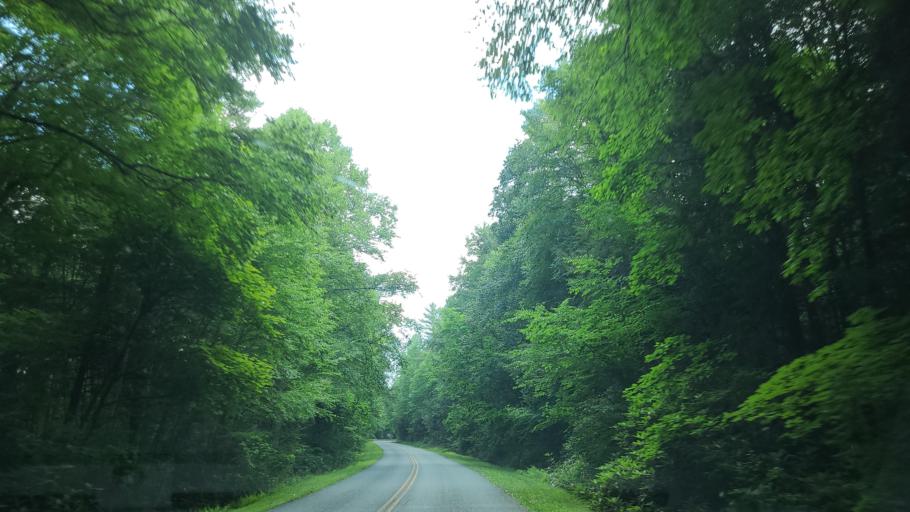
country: US
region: North Carolina
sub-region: Avery County
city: Newland
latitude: 35.9768
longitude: -81.9324
